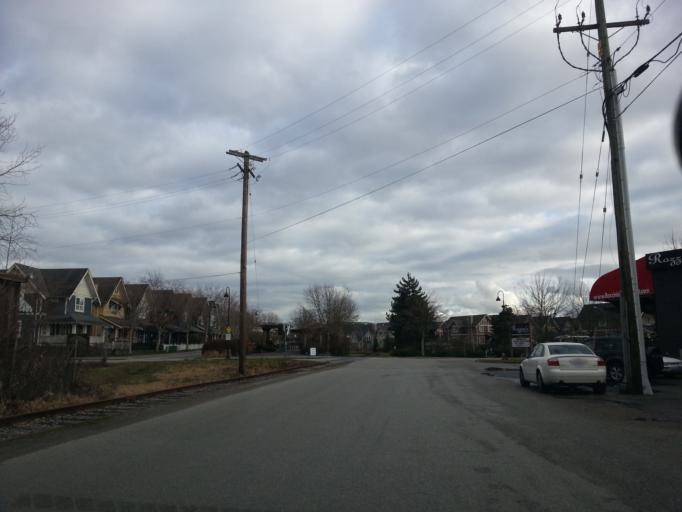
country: CA
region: British Columbia
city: New Westminster
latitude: 49.1949
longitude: -122.9283
